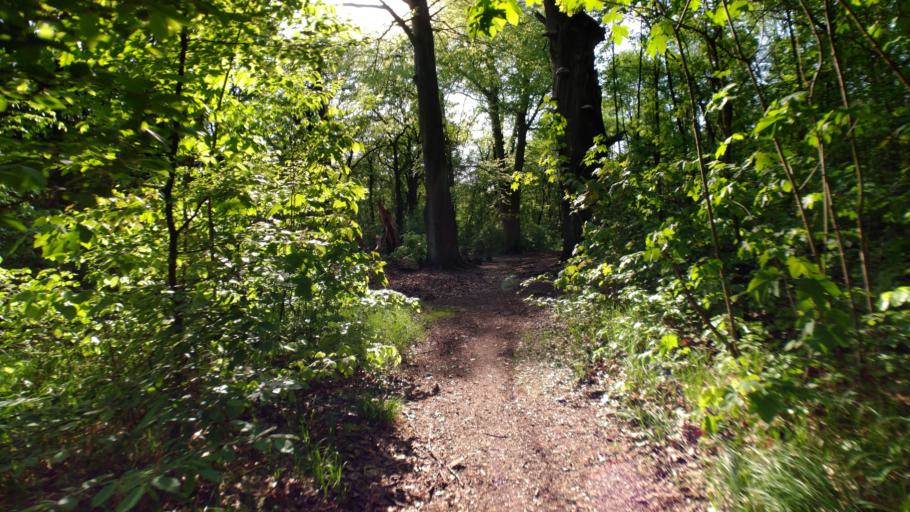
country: DE
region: Saxony
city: Albertstadt
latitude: 51.0775
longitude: 13.7887
